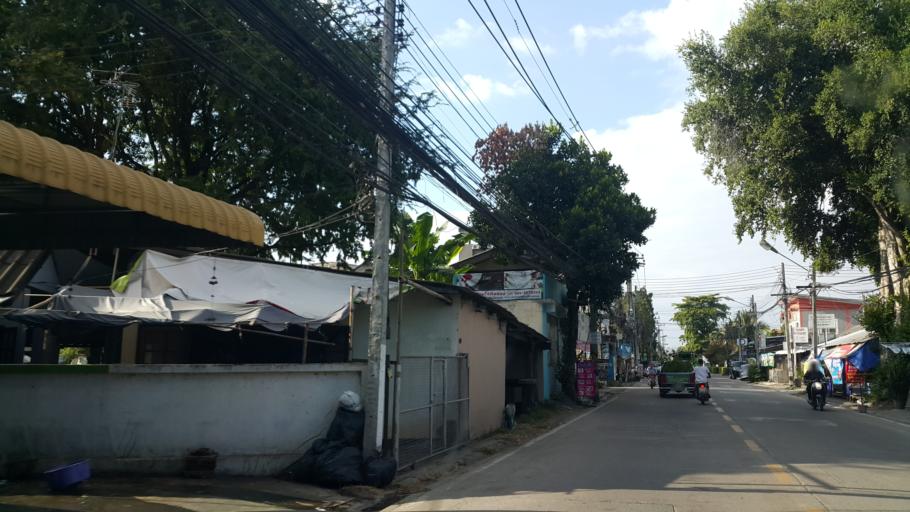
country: TH
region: Chiang Mai
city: Chiang Mai
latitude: 18.7956
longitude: 99.0171
